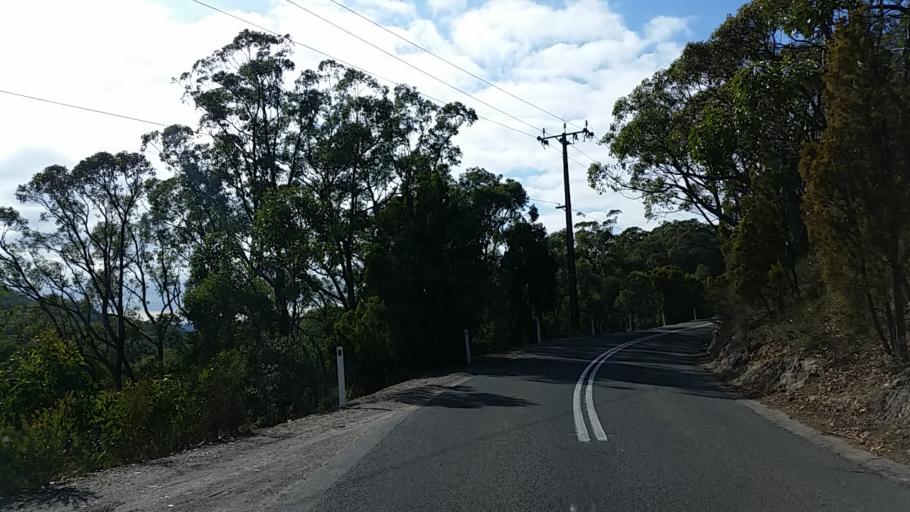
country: AU
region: South Australia
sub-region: Adelaide Hills
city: Crafers
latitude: -34.9722
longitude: 138.7081
